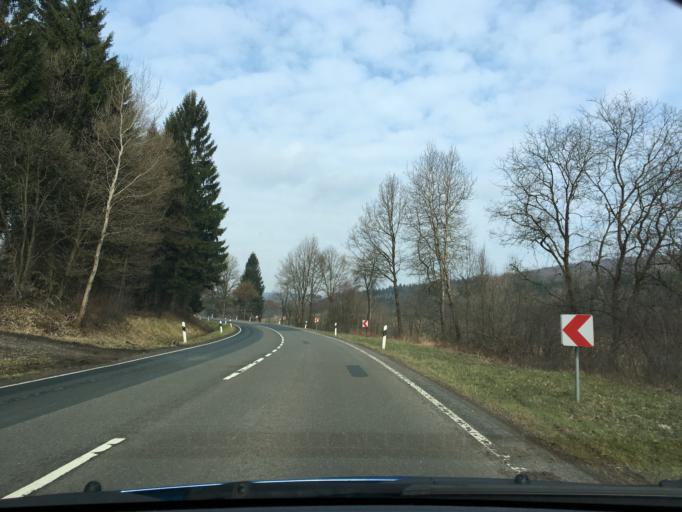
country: DE
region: Lower Saxony
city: Bodenfelde
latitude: 51.7151
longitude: 9.5305
